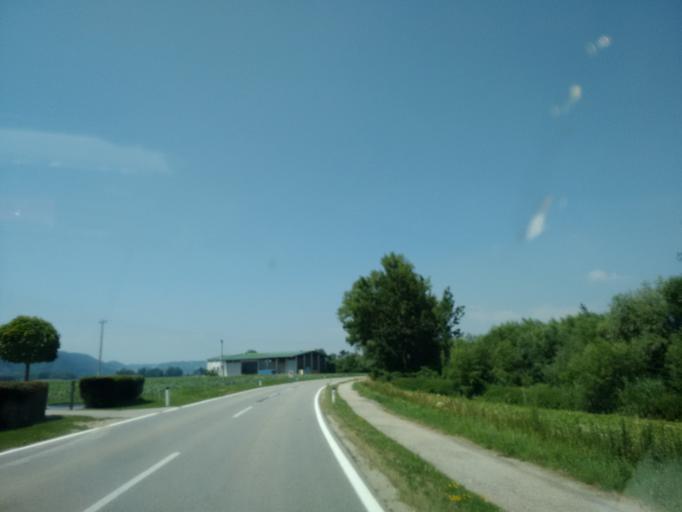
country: AT
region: Upper Austria
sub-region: Politischer Bezirk Urfahr-Umgebung
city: Feldkirchen an der Donau
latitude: 48.3198
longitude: 14.0121
